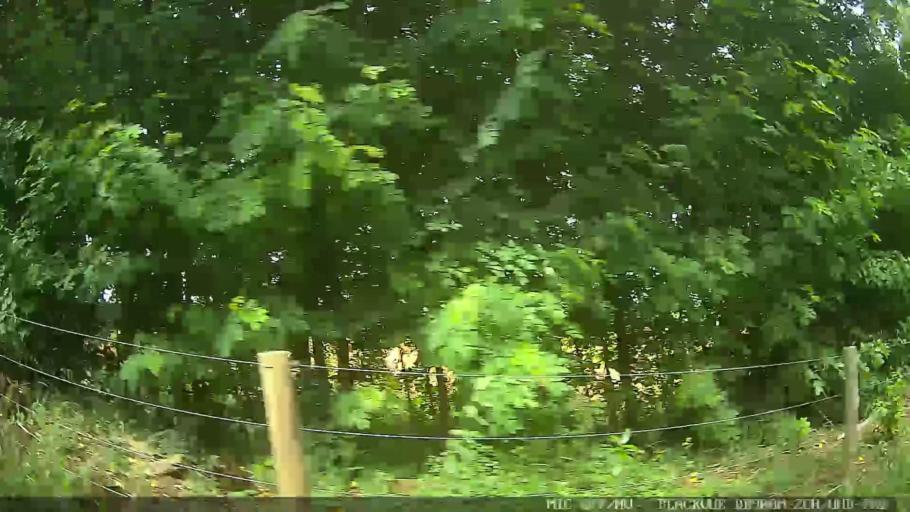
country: BR
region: Minas Gerais
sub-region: Extrema
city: Extrema
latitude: -22.8347
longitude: -46.2862
